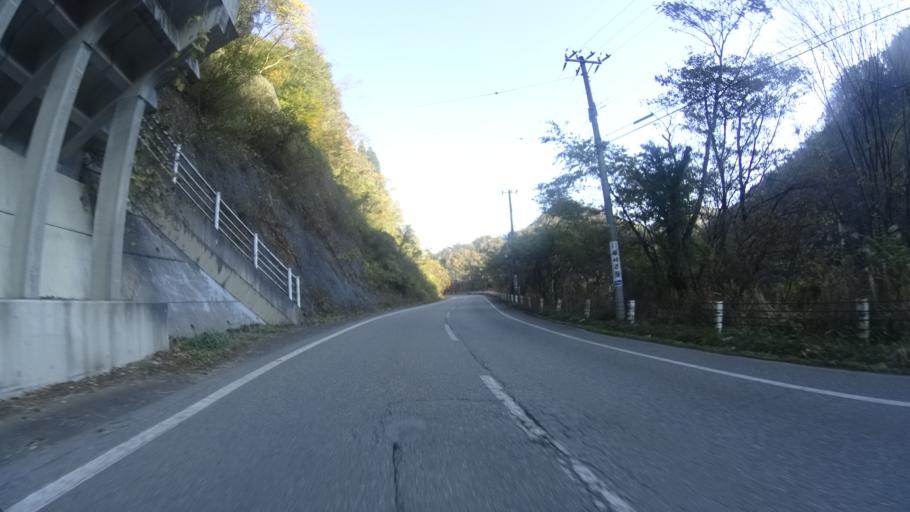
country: JP
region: Fukui
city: Maruoka
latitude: 36.2071
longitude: 136.3485
